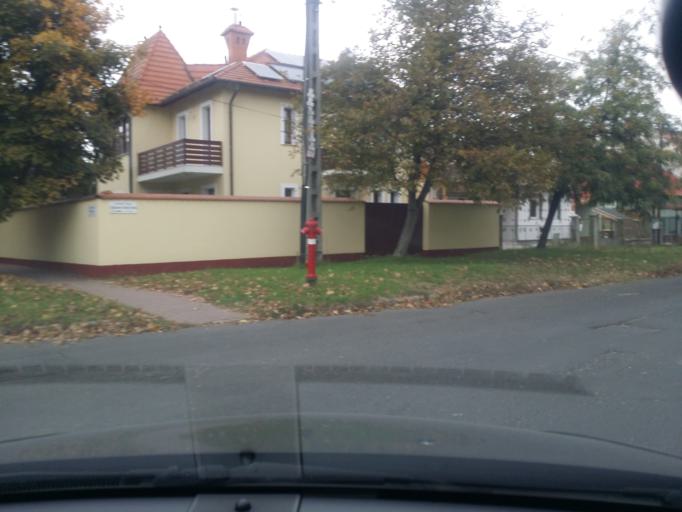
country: HU
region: Budapest
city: Budapest IV. keruelet
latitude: 47.5851
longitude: 19.0862
